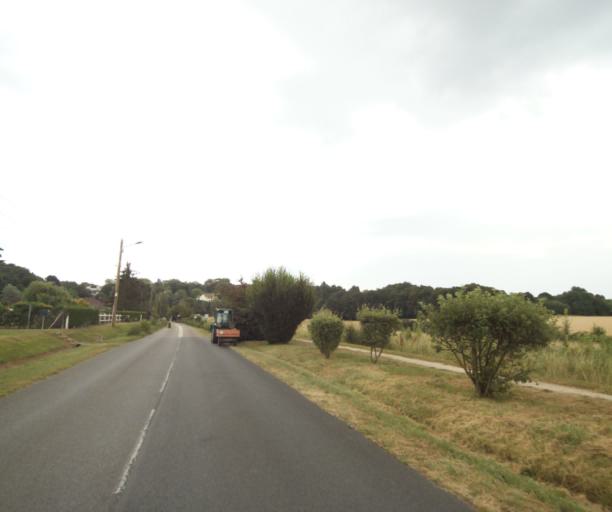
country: FR
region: Ile-de-France
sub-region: Departement de Seine-et-Marne
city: Saint-Sauveur-sur-Ecole
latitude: 48.4989
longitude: 2.5401
